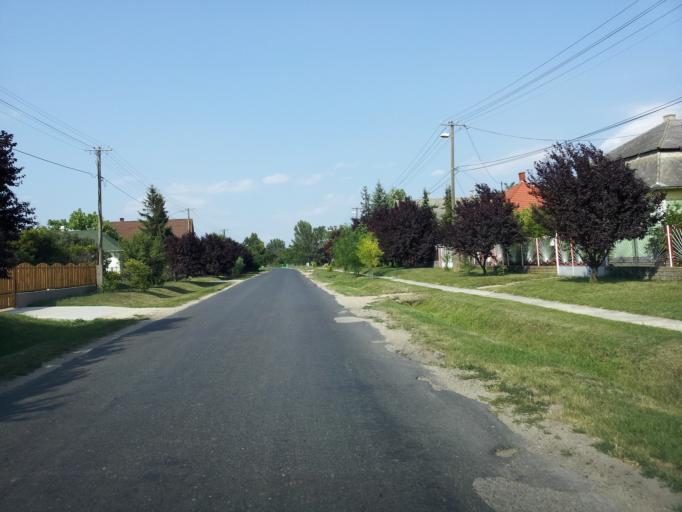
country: HU
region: Veszprem
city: Berhida
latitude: 47.0882
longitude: 18.0843
